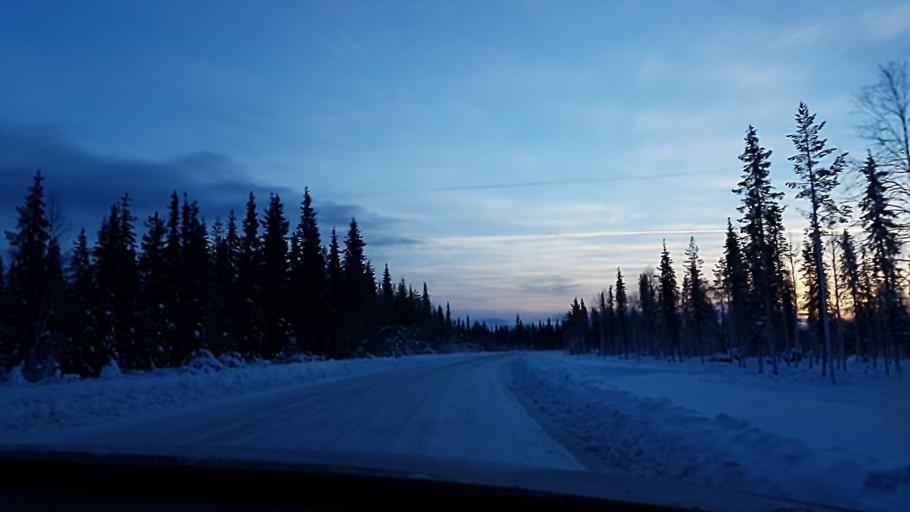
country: SE
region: Norrbotten
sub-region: Jokkmokks Kommun
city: Jokkmokk
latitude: 66.1002
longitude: 20.0666
